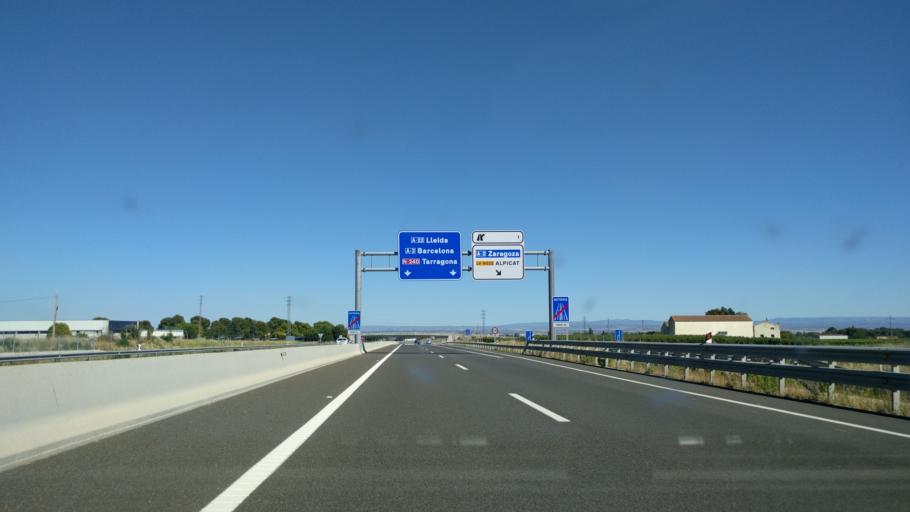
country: ES
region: Catalonia
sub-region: Provincia de Lleida
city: Alpicat
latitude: 41.6520
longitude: 0.5507
